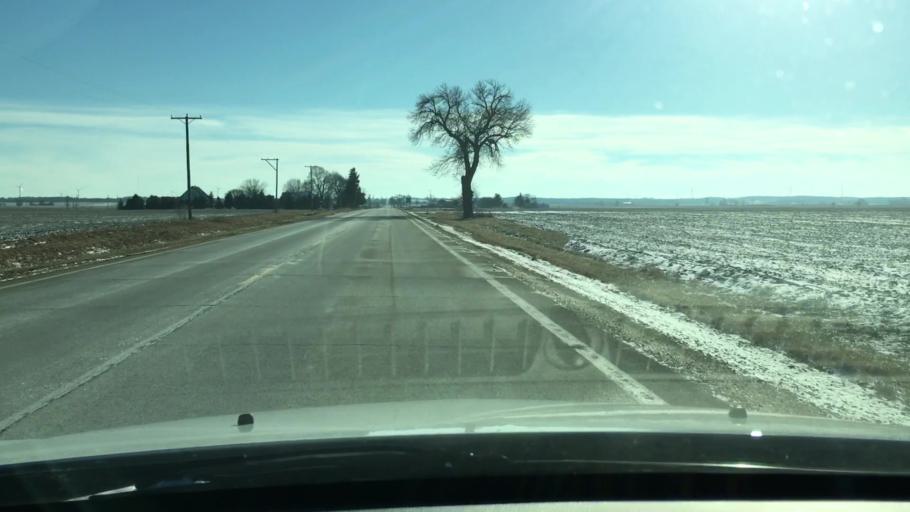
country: US
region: Illinois
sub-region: Ogle County
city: Rochelle
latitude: 41.7666
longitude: -89.0837
